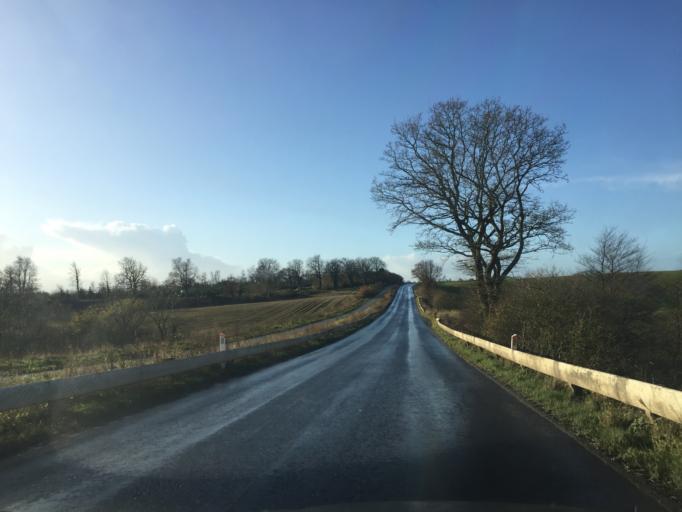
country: DK
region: South Denmark
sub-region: Kolding Kommune
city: Sonder Bjert
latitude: 55.4662
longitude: 9.5915
